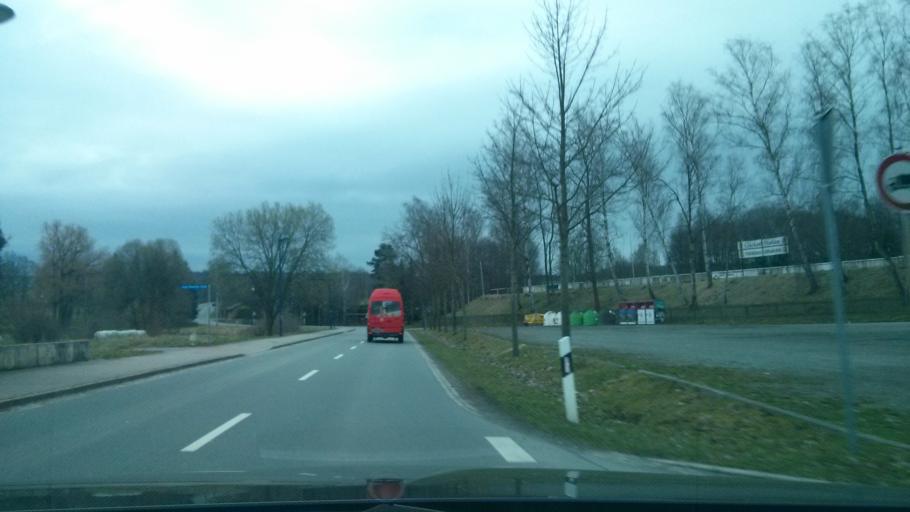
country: DE
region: Saxony
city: Oelsnitz
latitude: 50.7211
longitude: 12.7022
